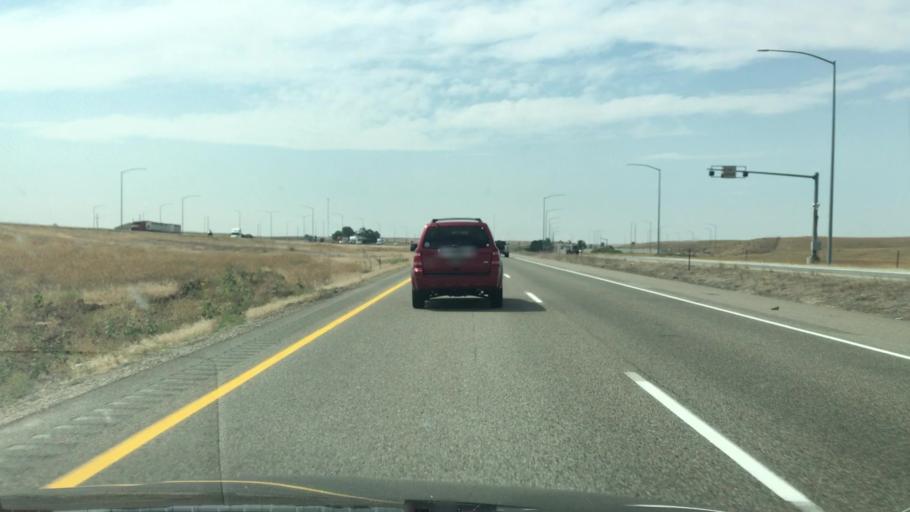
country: US
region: Idaho
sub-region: Ada County
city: Boise
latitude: 43.4285
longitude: -116.0511
